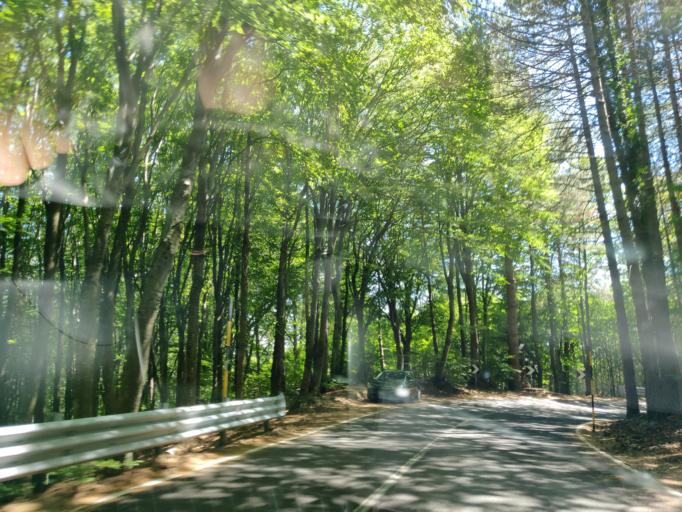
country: IT
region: Tuscany
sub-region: Provincia di Siena
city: Abbadia San Salvatore
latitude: 42.9031
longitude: 11.6522
